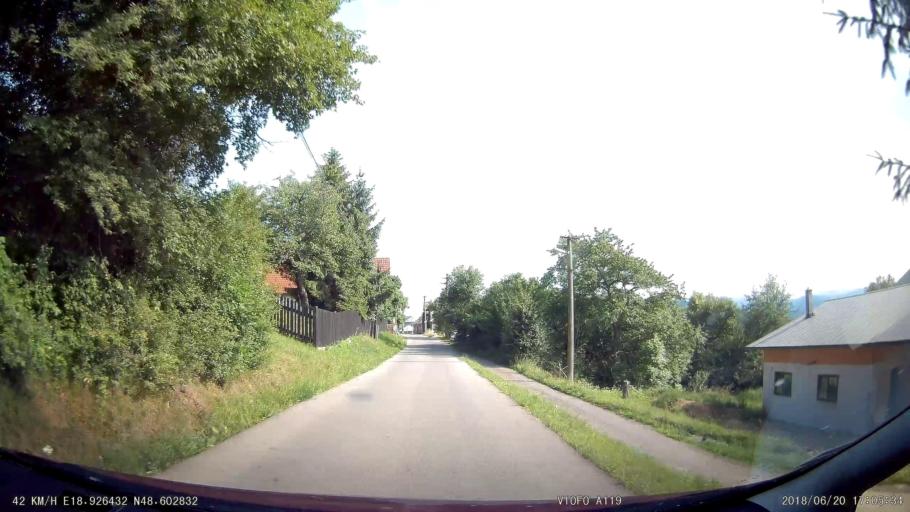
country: SK
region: Banskobystricky
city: Ziar nad Hronom
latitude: 48.6028
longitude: 18.9265
